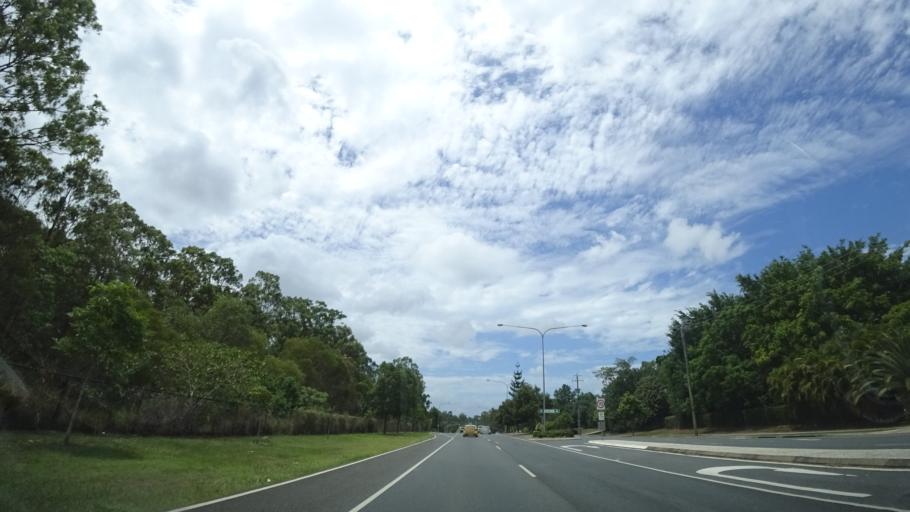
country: AU
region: Queensland
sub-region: Brisbane
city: Bridegman Downs
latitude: -27.3462
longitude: 152.9968
